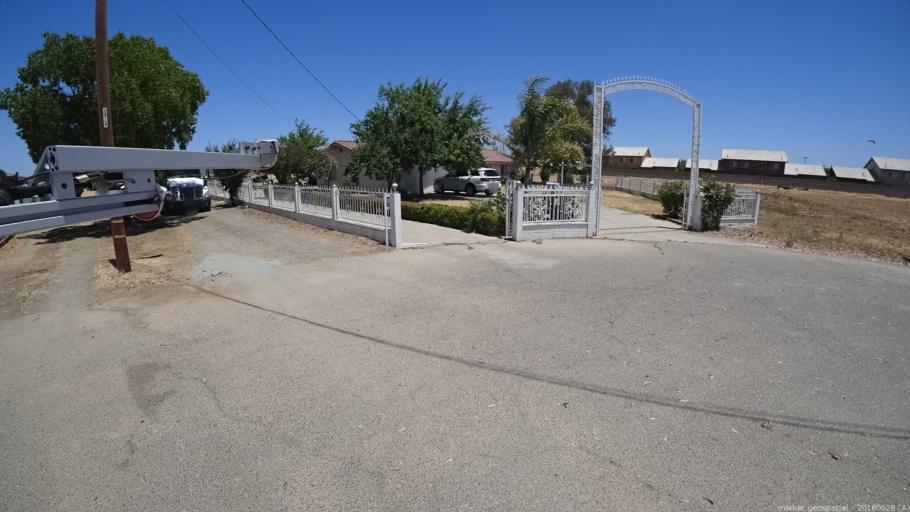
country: US
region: California
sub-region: Madera County
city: Parksdale
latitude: 36.9473
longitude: -120.0251
